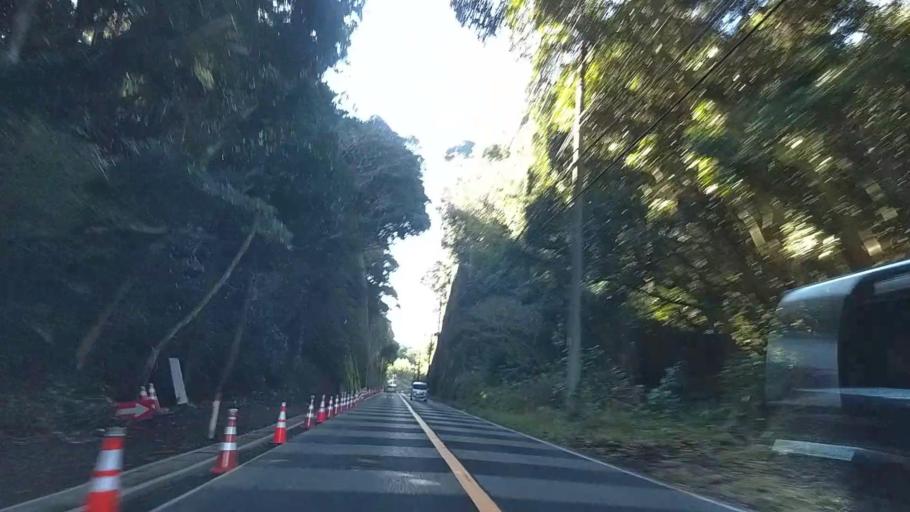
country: JP
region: Chiba
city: Tateyama
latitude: 34.9618
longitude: 139.8551
